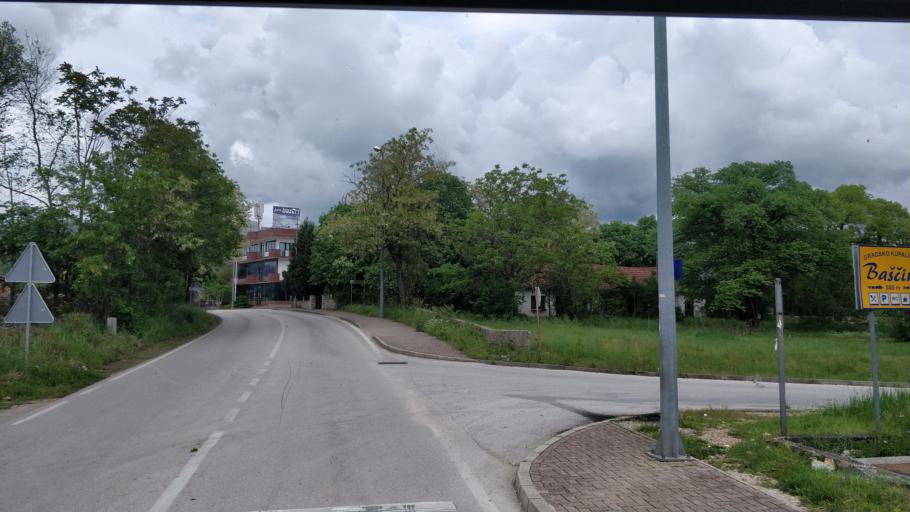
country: BA
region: Federation of Bosnia and Herzegovina
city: Ljubuski
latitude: 43.1841
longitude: 17.5278
